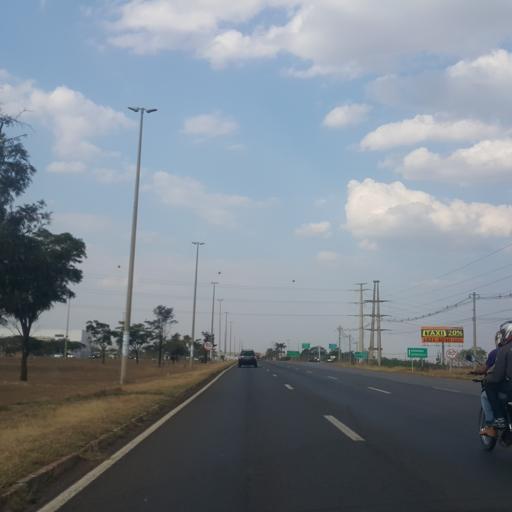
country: BR
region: Federal District
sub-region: Brasilia
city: Brasilia
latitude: -15.8842
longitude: -48.0659
